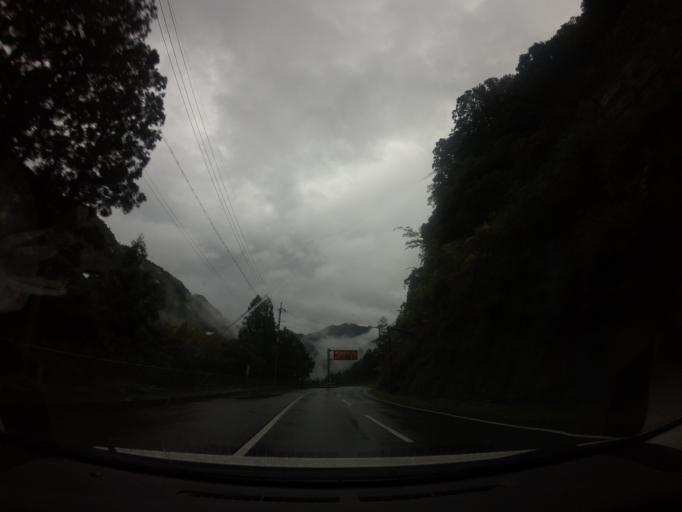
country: JP
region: Wakayama
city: Koya
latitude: 34.0066
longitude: 135.7936
